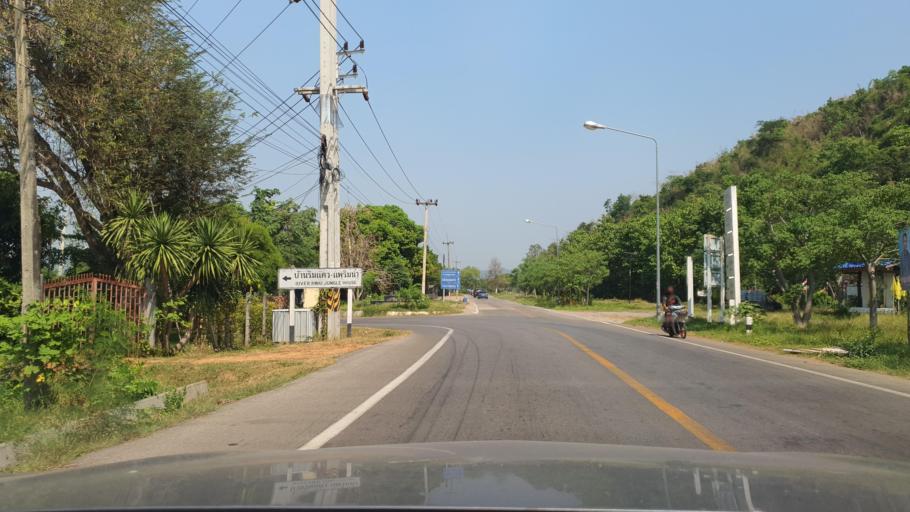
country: TH
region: Kanchanaburi
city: Sai Yok
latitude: 14.0937
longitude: 99.1788
